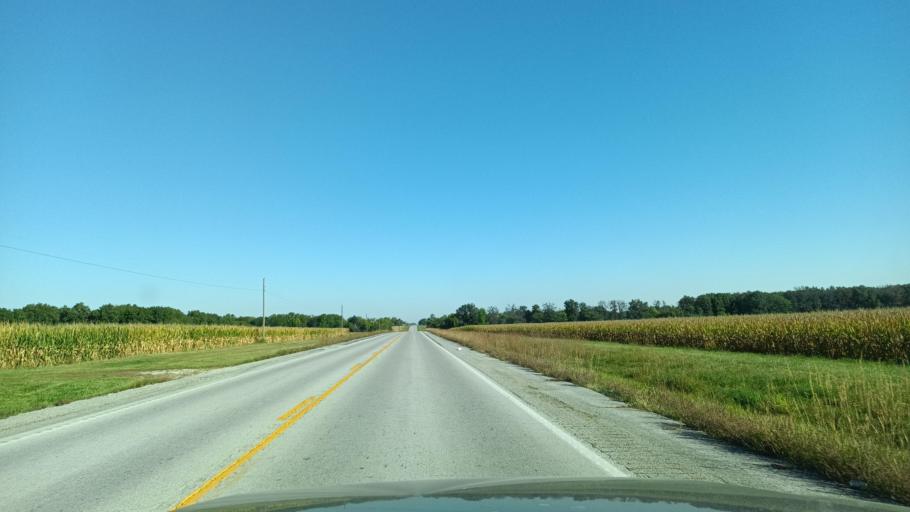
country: US
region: Missouri
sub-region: Audrain County
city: Vandalia
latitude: 39.3310
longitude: -91.6430
